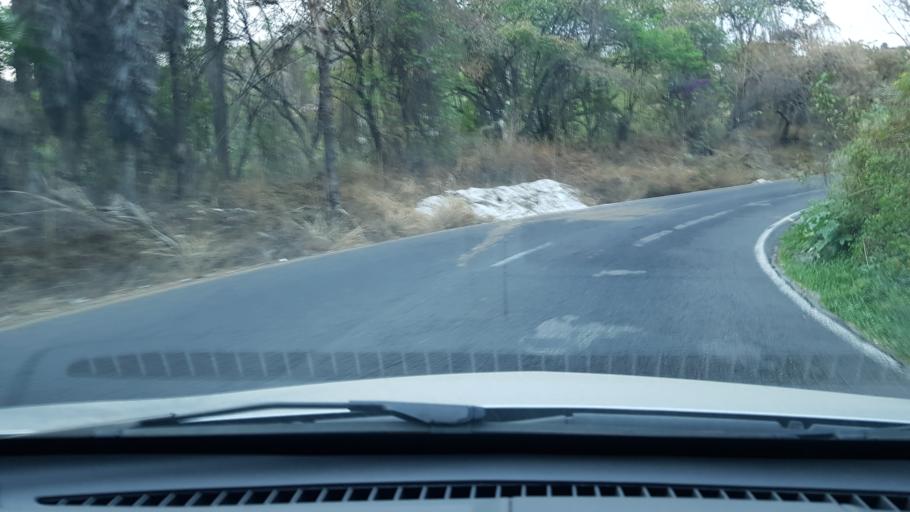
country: MX
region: Morelos
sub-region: Jiutepec
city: Independencia
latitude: 18.8768
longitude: -99.1207
